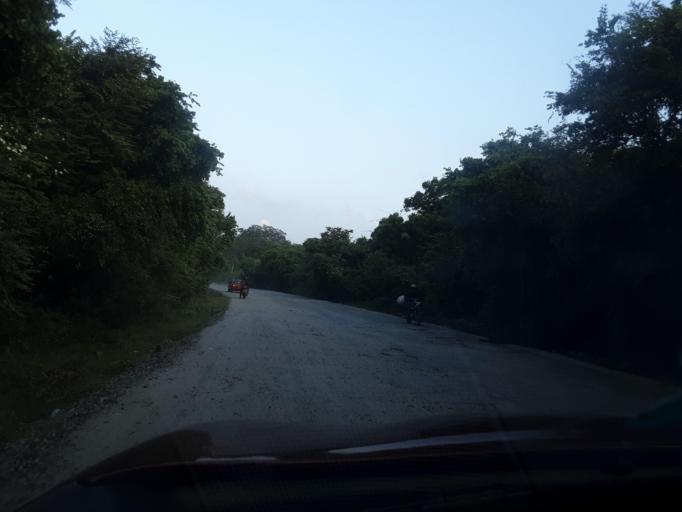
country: LK
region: Central
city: Dambulla
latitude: 7.8102
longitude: 80.7696
